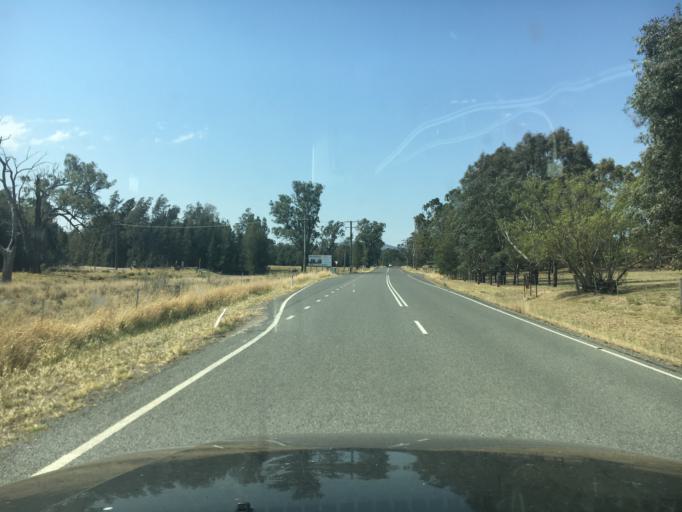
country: AU
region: New South Wales
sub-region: Singleton
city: Singleton
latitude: -32.5463
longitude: 151.2408
